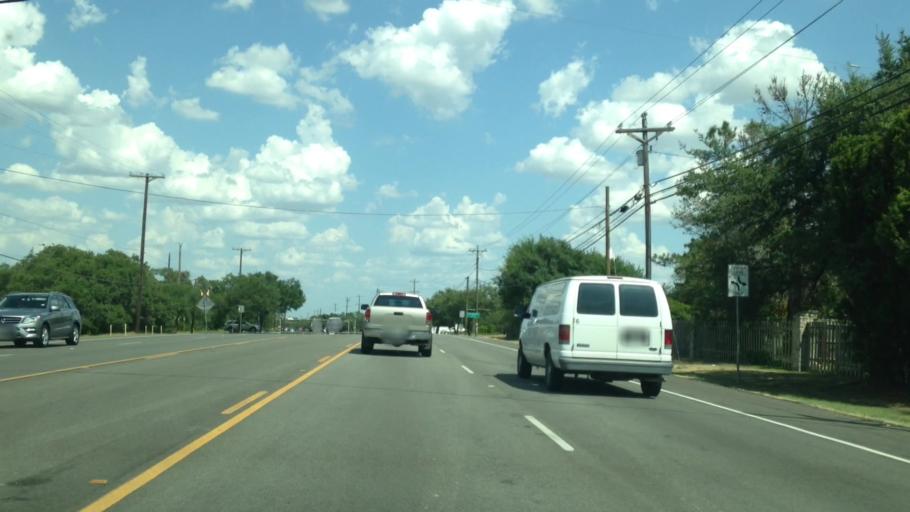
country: US
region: Texas
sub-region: Williamson County
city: Georgetown
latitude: 30.6330
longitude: -97.7144
